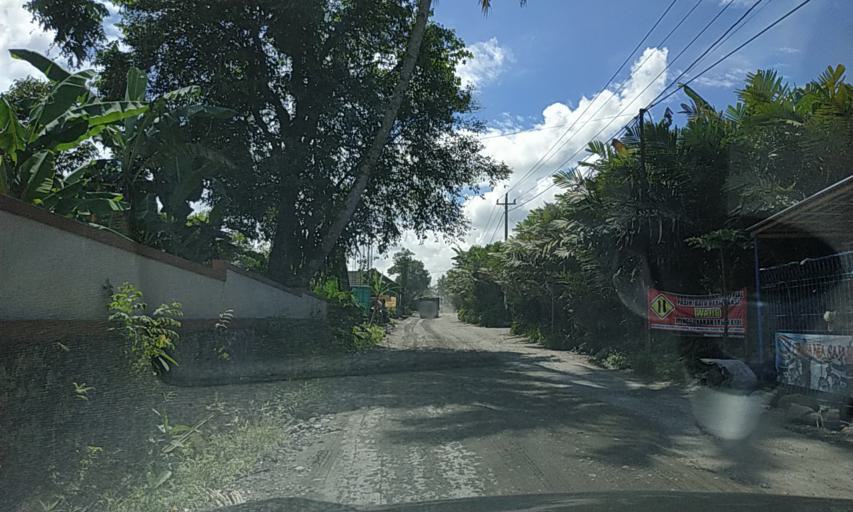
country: ID
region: Central Java
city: Muntilan
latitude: -7.6035
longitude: 110.3581
